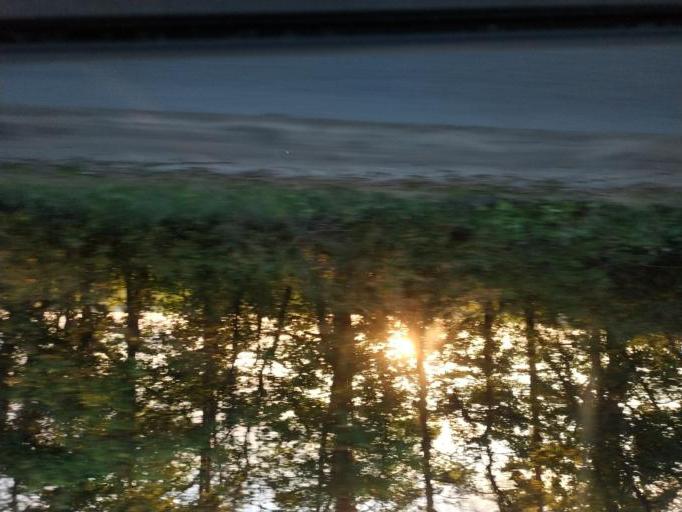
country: RU
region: Moskovskaya
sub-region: Shchelkovskiy Rayon
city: Grebnevo
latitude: 56.0089
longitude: 38.1471
